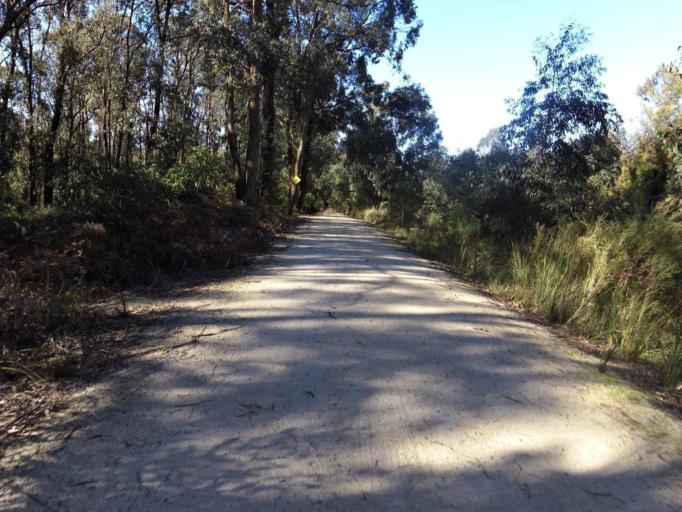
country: AU
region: Victoria
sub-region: Latrobe
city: Moe
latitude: -38.3734
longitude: 146.2005
